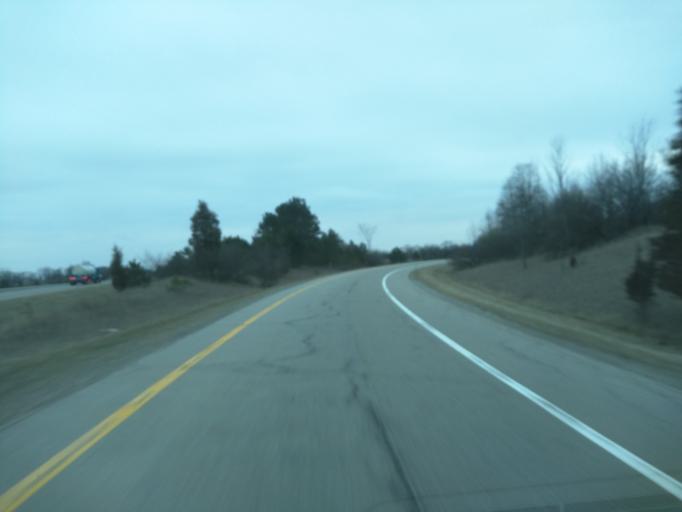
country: US
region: Michigan
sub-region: Ingham County
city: Leslie
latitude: 42.3819
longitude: -84.4294
